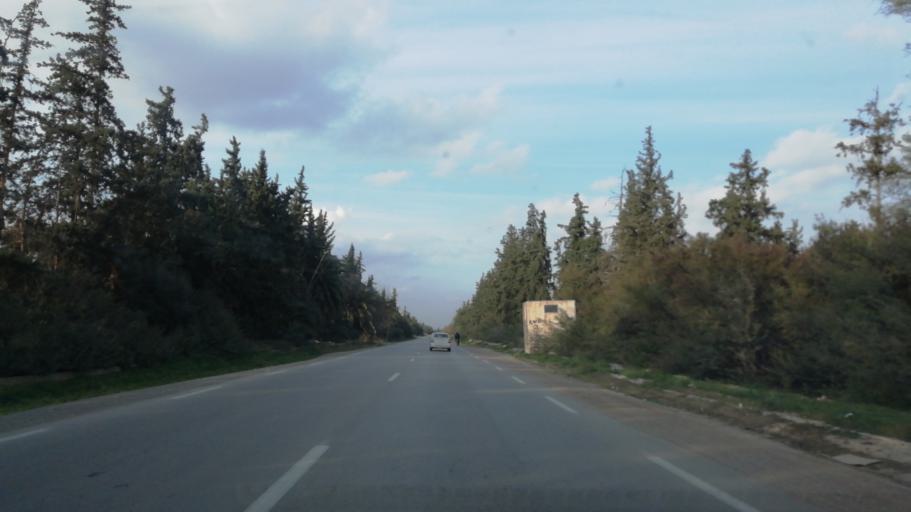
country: DZ
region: Mascara
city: Mascara
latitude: 35.6050
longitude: 0.0525
